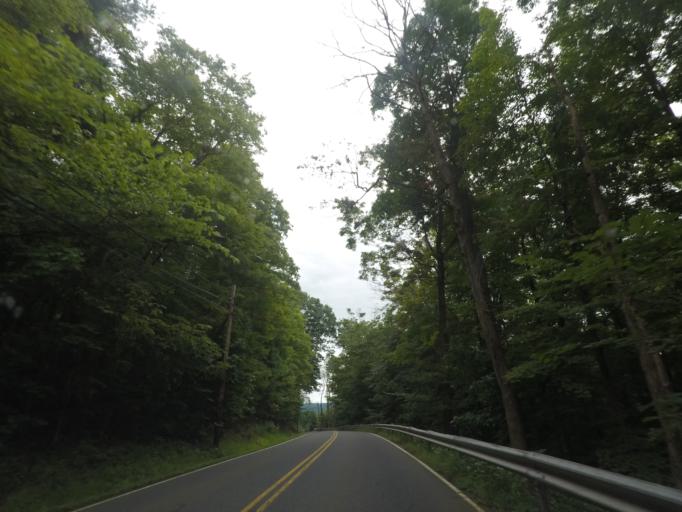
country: US
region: New York
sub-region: Rensselaer County
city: Nassau
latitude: 42.4735
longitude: -73.5903
